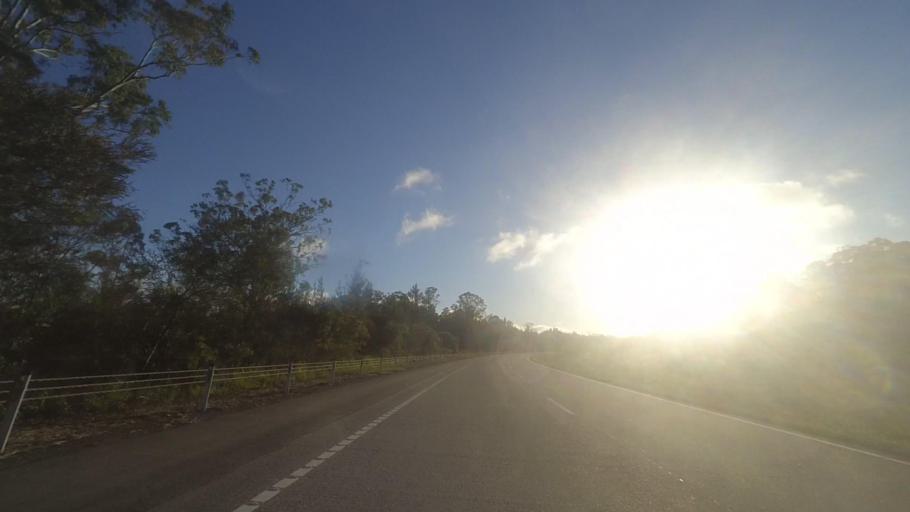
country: AU
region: New South Wales
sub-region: Great Lakes
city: Hawks Nest
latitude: -32.5458
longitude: 152.1616
